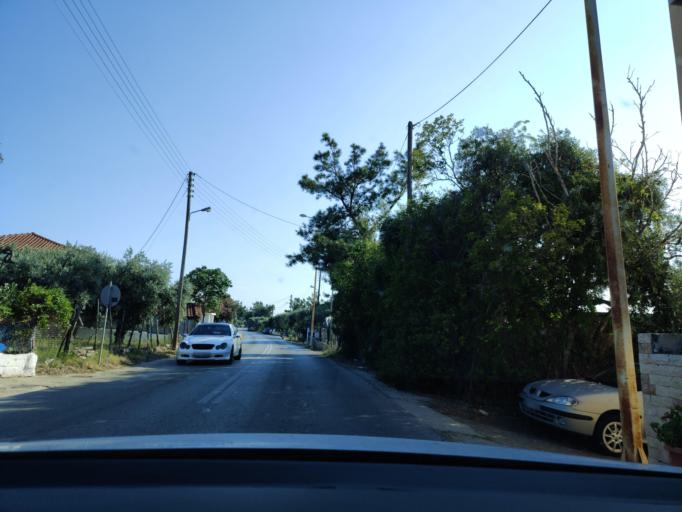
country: GR
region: East Macedonia and Thrace
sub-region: Nomos Kavalas
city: Prinos
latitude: 40.7021
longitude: 24.5295
